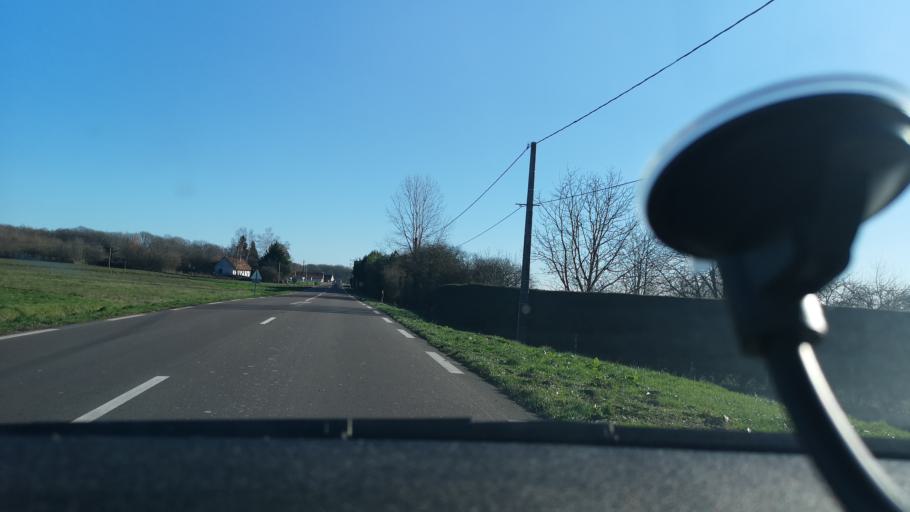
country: FR
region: Bourgogne
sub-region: Departement de Saone-et-Loire
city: Ouroux-sur-Saone
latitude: 46.7717
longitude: 4.9719
